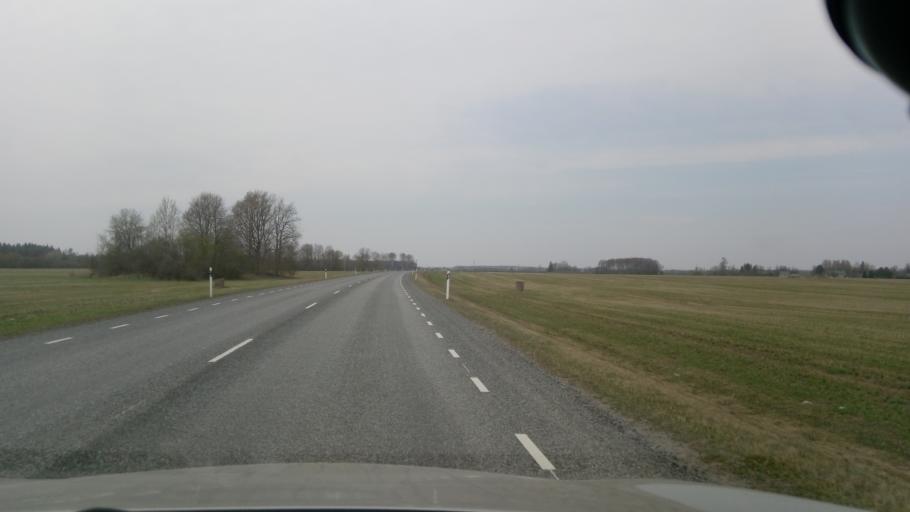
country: EE
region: Jaervamaa
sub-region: Tueri vald
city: Sarevere
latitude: 58.7680
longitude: 25.5284
